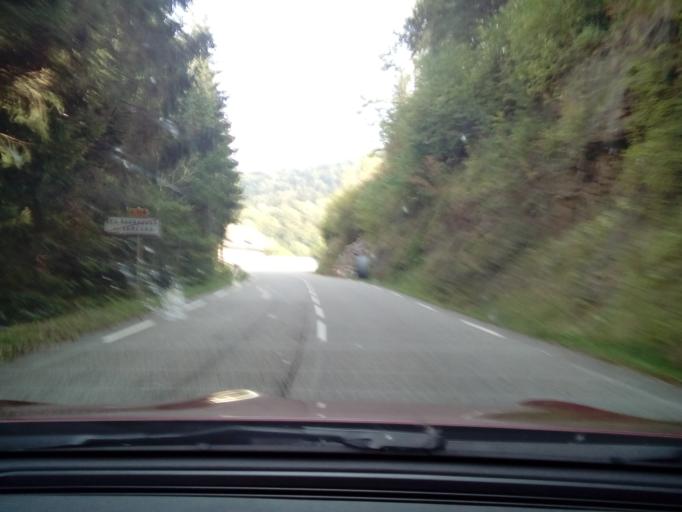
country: FR
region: Rhone-Alpes
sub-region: Departement de la Drome
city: Saint-Laurent-en-Royans
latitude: 45.0015
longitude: 5.4217
